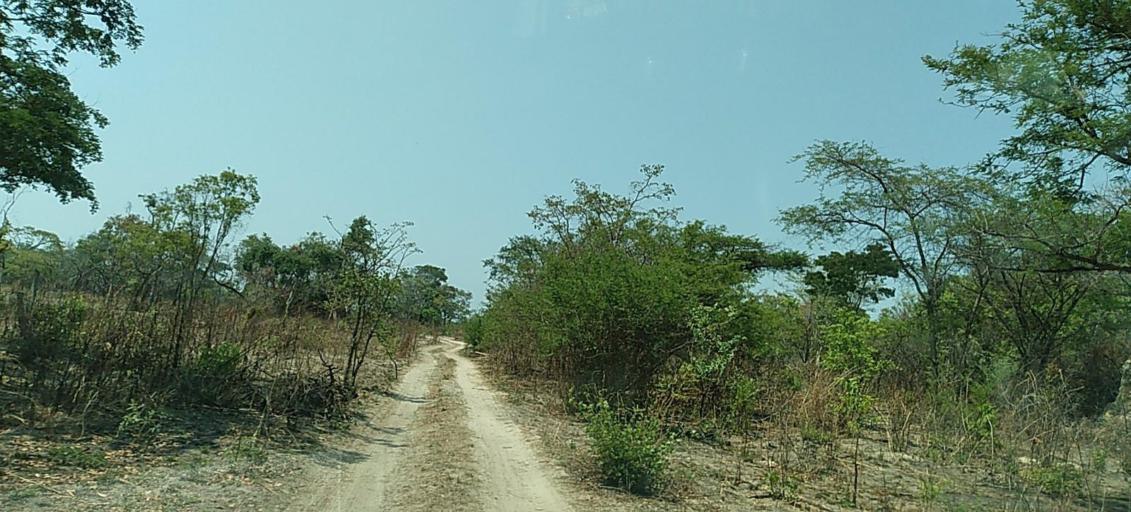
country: ZM
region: Copperbelt
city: Mpongwe
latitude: -13.8386
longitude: 28.0595
